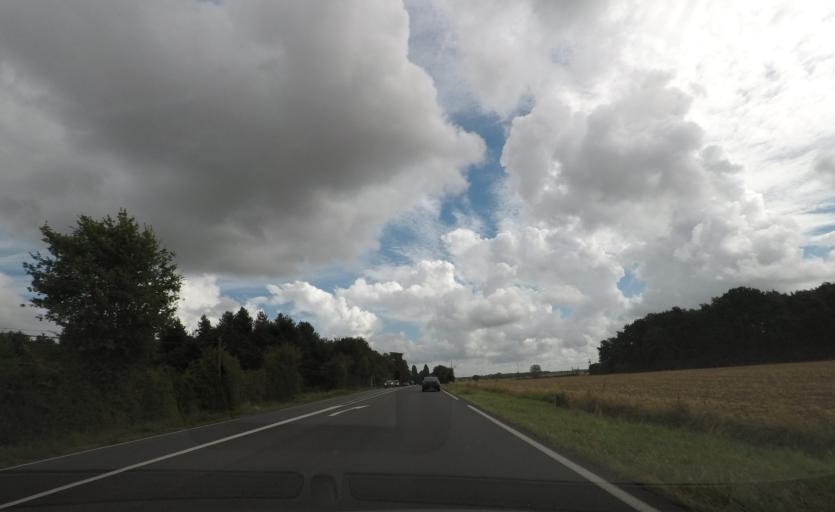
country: FR
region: Pays de la Loire
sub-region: Departement de Maine-et-Loire
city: Pellouailles-les-Vignes
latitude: 47.5323
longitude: -0.4166
